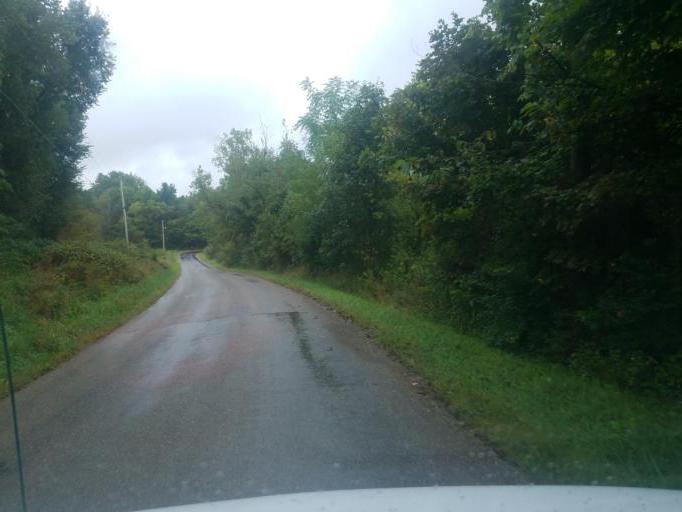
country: US
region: Ohio
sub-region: Wayne County
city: West Salem
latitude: 40.9317
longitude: -82.1260
